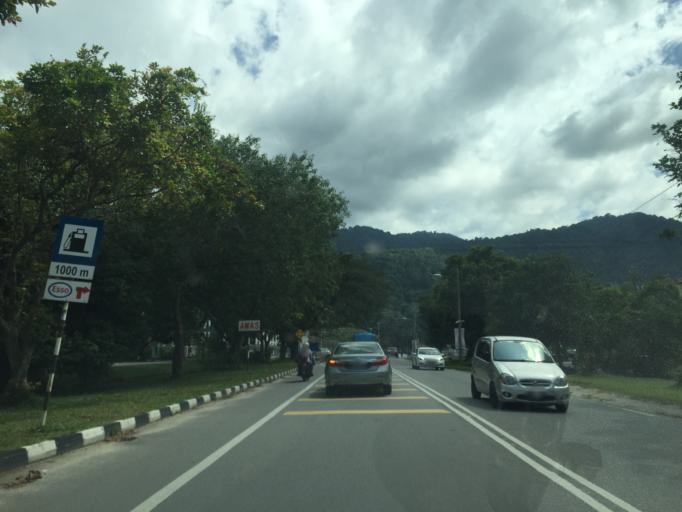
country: MY
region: Perak
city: Kampar
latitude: 4.3250
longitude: 101.1497
